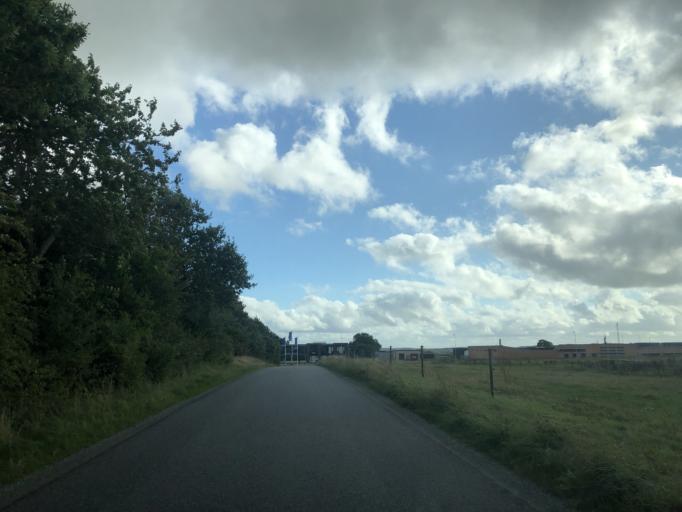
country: DK
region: South Denmark
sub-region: Vejle Kommune
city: Borkop
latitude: 55.6762
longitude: 9.5982
